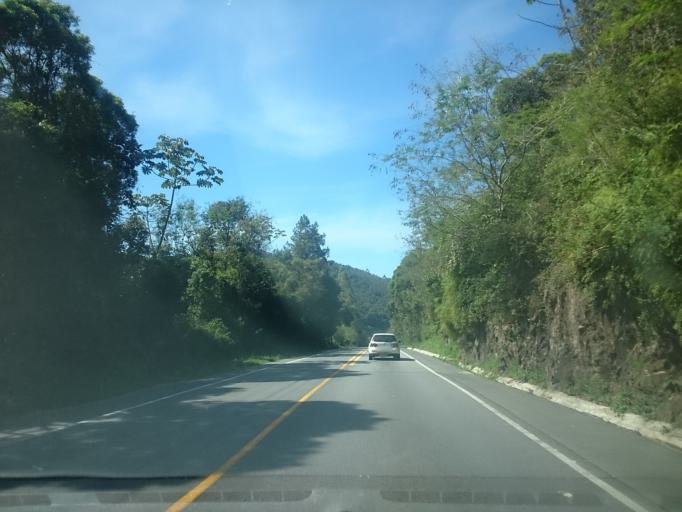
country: BR
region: Santa Catarina
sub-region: Santo Amaro Da Imperatriz
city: Santo Amaro da Imperatriz
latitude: -27.7214
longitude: -48.9047
